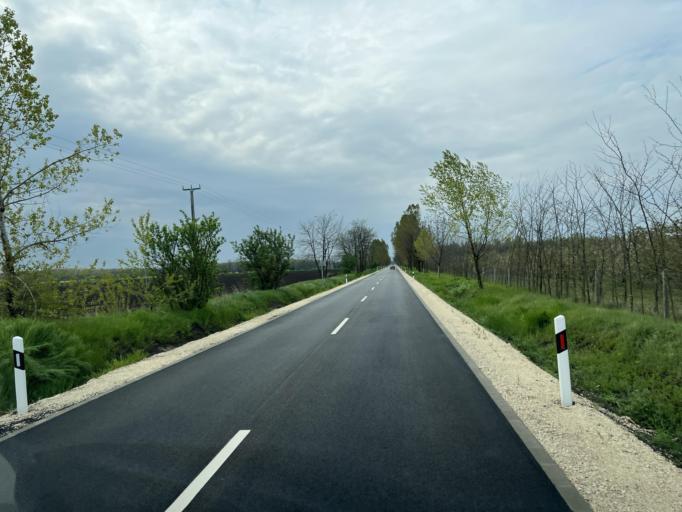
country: HU
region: Pest
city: Nyaregyhaza
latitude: 47.2388
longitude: 19.5199
